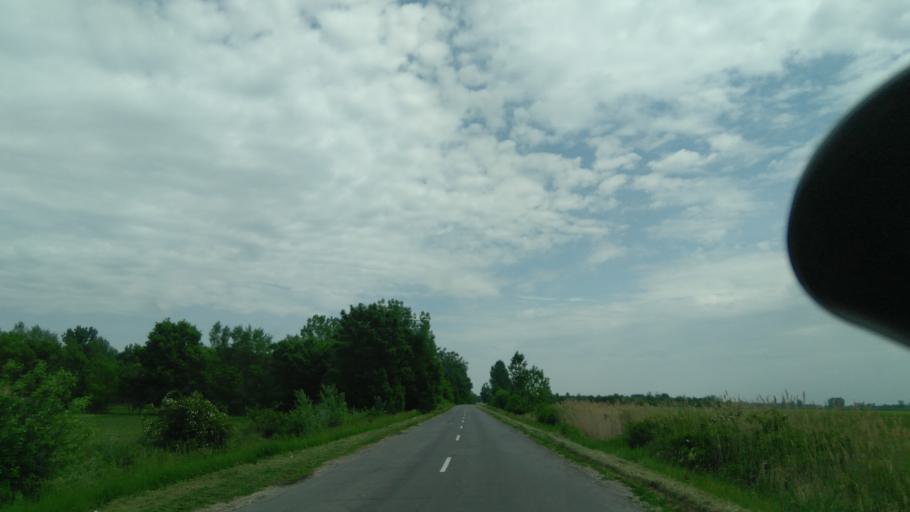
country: HU
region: Hajdu-Bihar
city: Komadi
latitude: 47.0182
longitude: 21.5292
